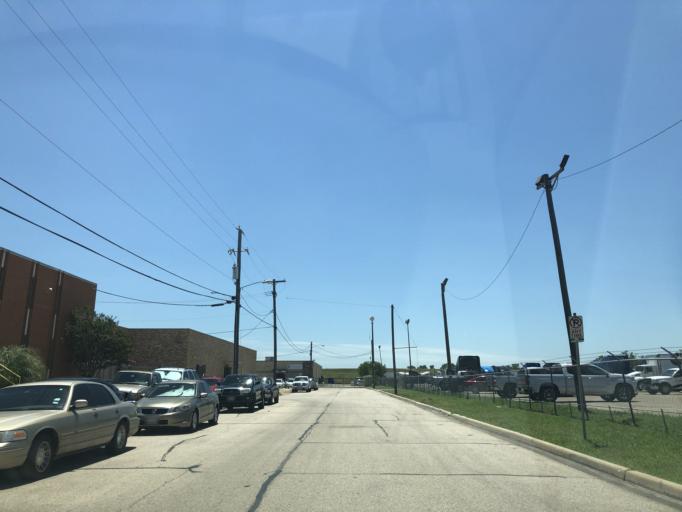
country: US
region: Texas
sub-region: Dallas County
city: Irving
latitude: 32.8056
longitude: -96.8861
